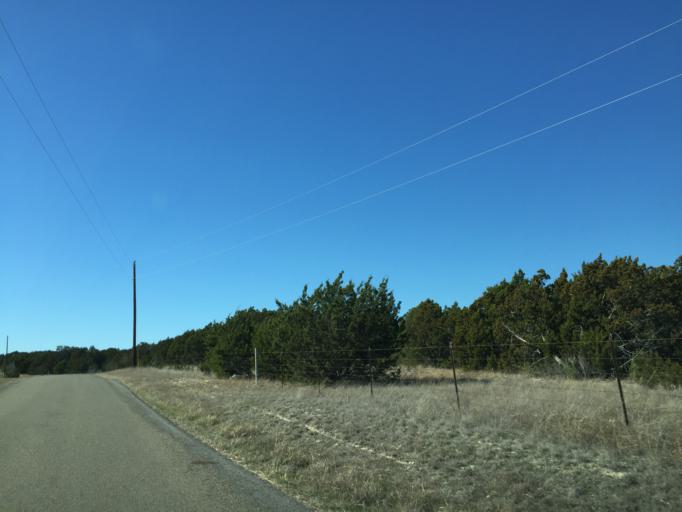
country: US
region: Texas
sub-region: Burnet County
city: Bertram
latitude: 30.9038
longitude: -98.1134
